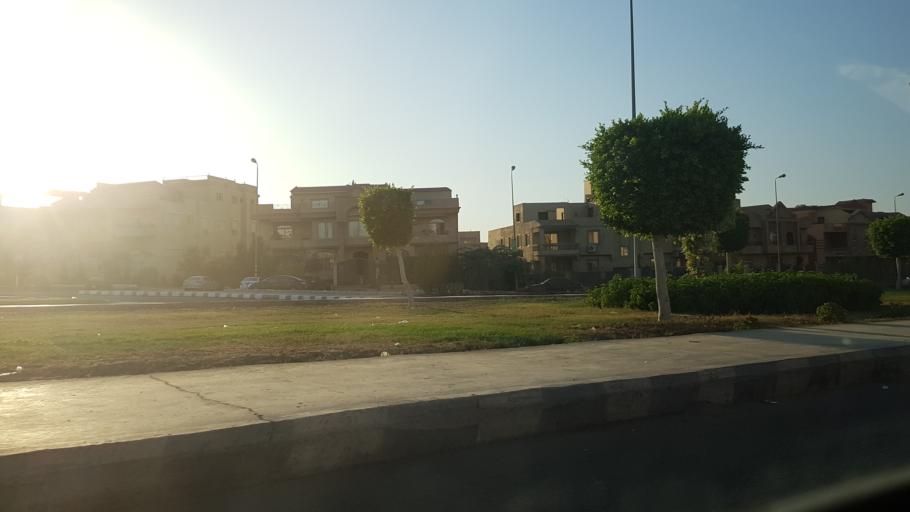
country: EG
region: Muhafazat al Qalyubiyah
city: Al Khankah
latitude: 30.0417
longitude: 31.4408
